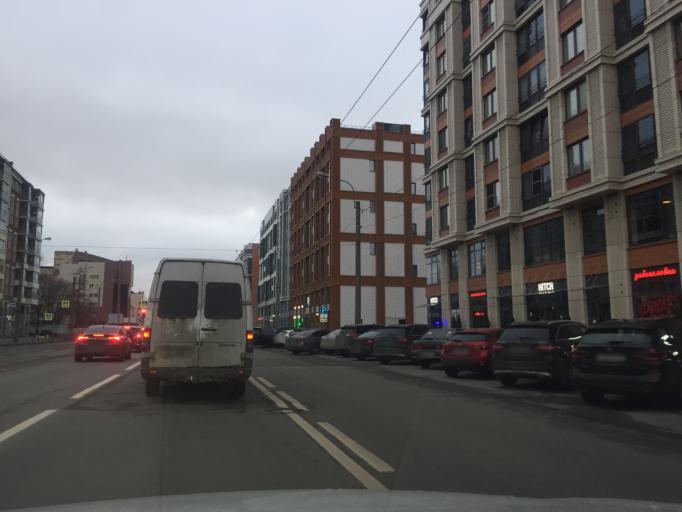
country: RU
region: St.-Petersburg
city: Petrogradka
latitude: 59.9757
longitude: 30.3175
